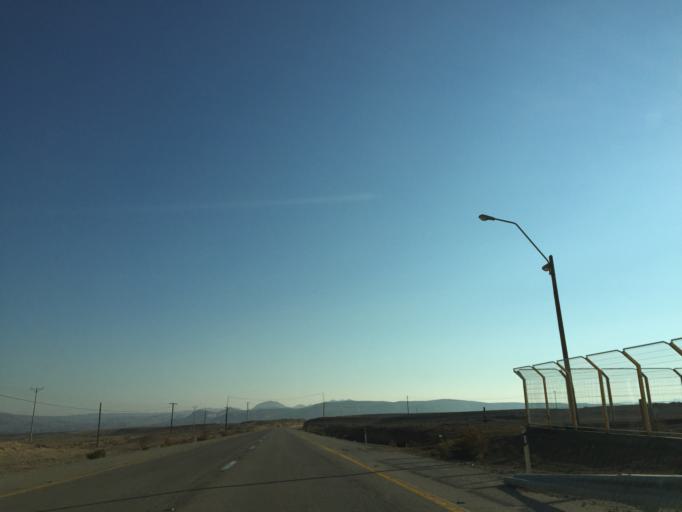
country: IL
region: Southern District
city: Mitzpe Ramon
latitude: 30.2889
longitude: 34.9899
